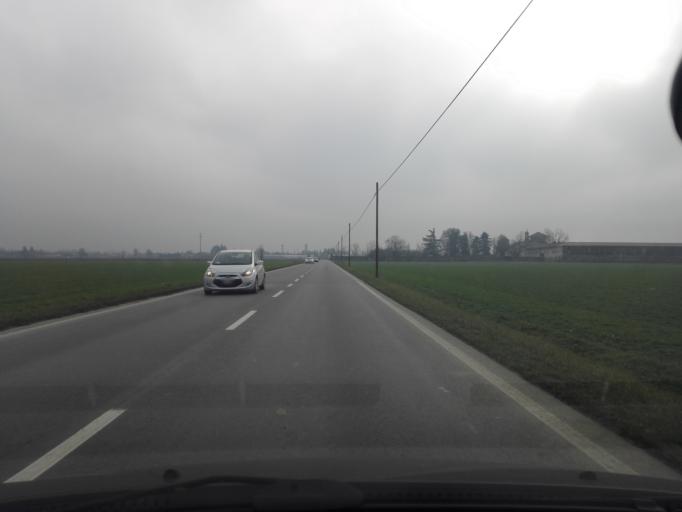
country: IT
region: Piedmont
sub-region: Provincia di Alessandria
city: Casal Cermelli
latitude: 44.8477
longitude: 8.6153
